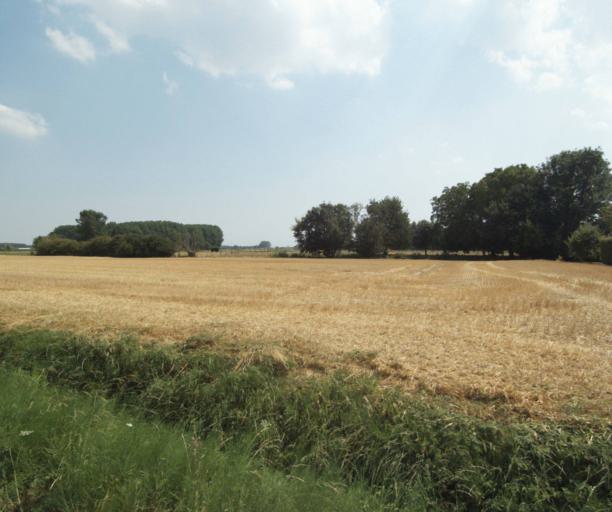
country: FR
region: Nord-Pas-de-Calais
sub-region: Departement du Nord
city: Quesnoy-sur-Deule
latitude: 50.7052
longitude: 3.0170
